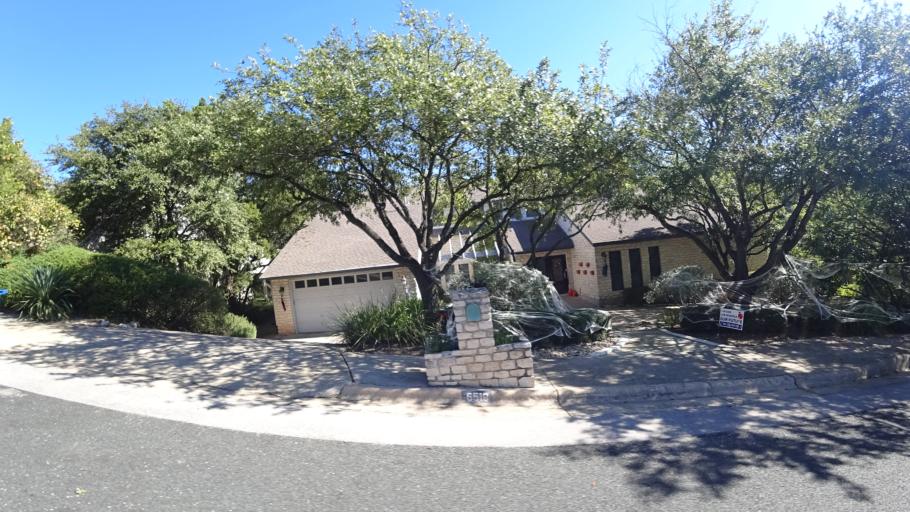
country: US
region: Texas
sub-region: Travis County
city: West Lake Hills
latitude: 30.3619
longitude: -97.7818
